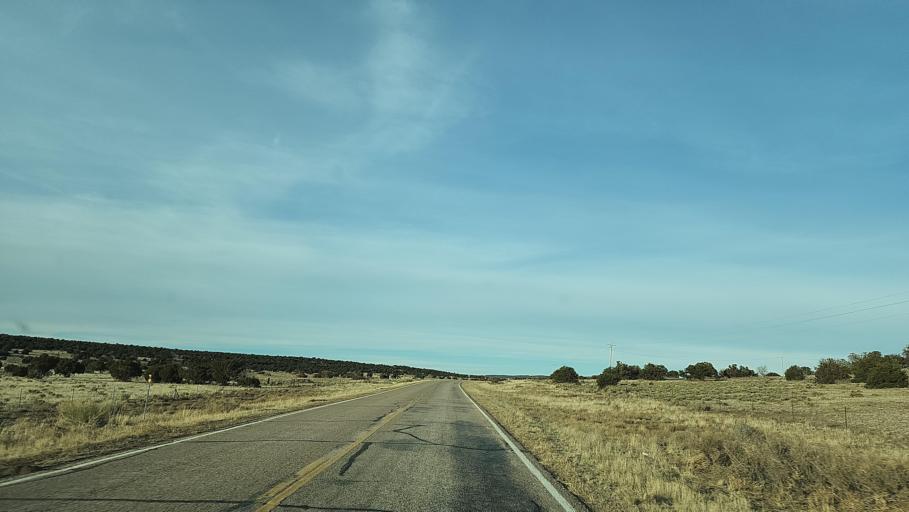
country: US
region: New Mexico
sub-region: Catron County
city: Reserve
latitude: 34.3961
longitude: -108.4451
